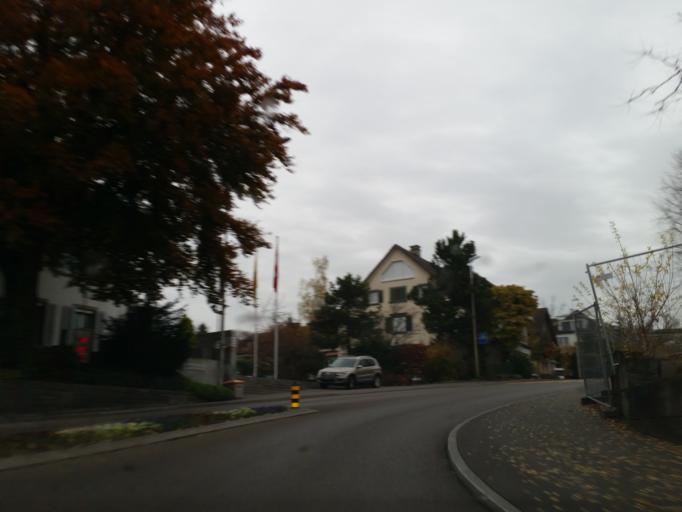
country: CH
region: Zurich
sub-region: Bezirk Meilen
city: Herrliberg
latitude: 47.2850
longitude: 8.6109
